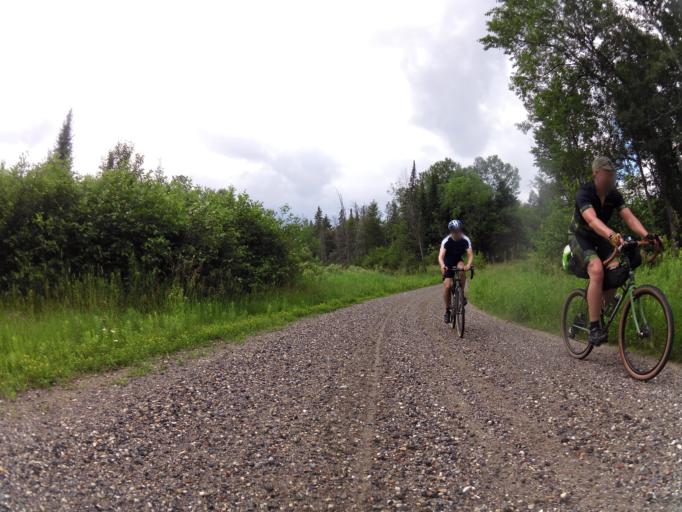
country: CA
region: Ontario
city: Renfrew
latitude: 45.0739
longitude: -76.7413
